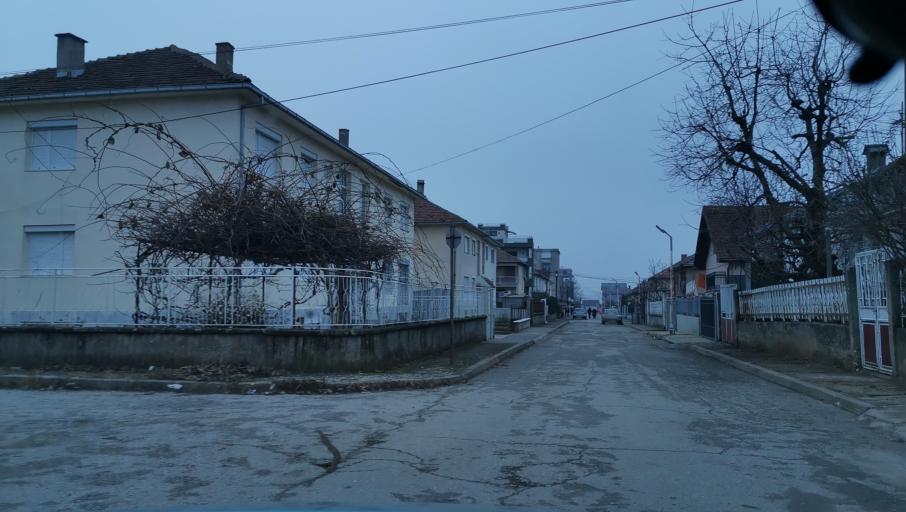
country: MK
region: Debar
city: Debar
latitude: 41.5154
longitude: 20.5319
